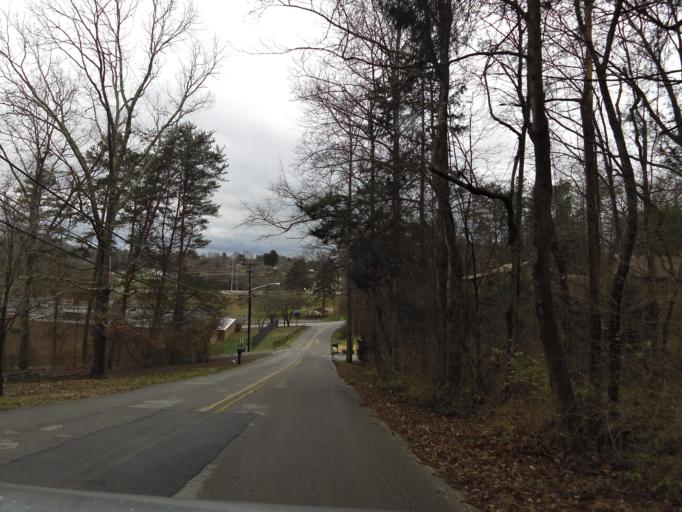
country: US
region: Tennessee
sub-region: Knox County
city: Knoxville
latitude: 35.9878
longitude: -84.0315
